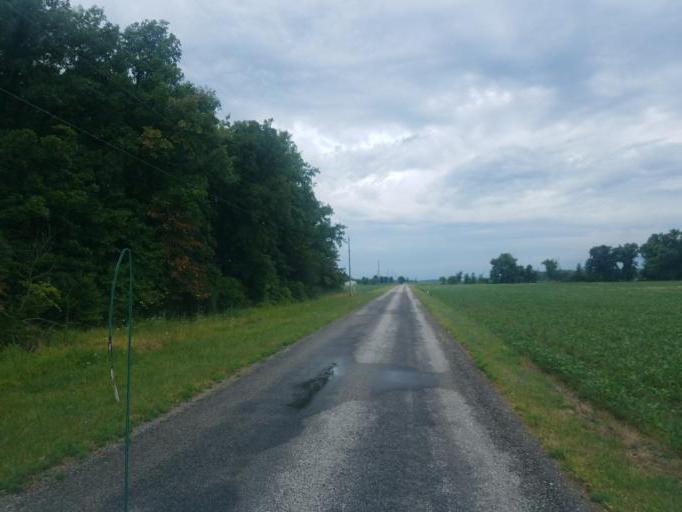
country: US
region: Ohio
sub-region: Paulding County
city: Antwerp
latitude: 41.2412
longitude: -84.6960
